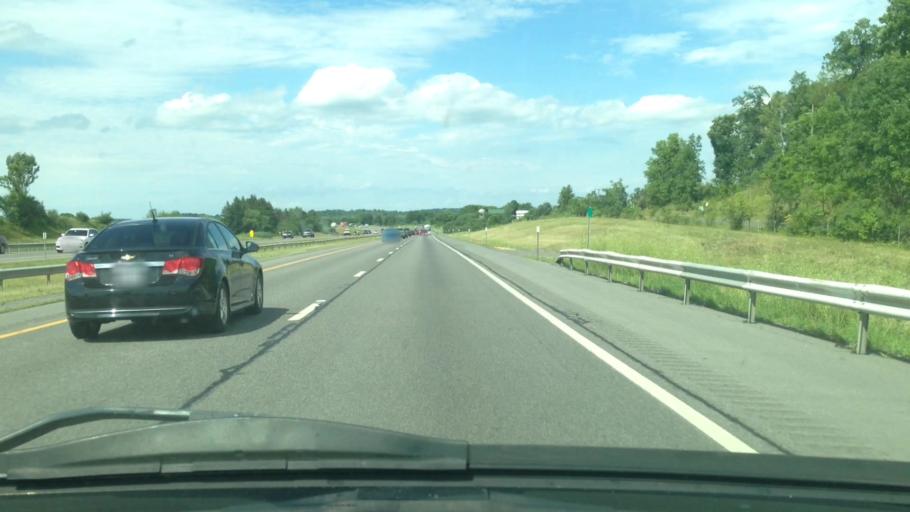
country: US
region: New York
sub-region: Cayuga County
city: Centerport
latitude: 43.0543
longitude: -76.5991
